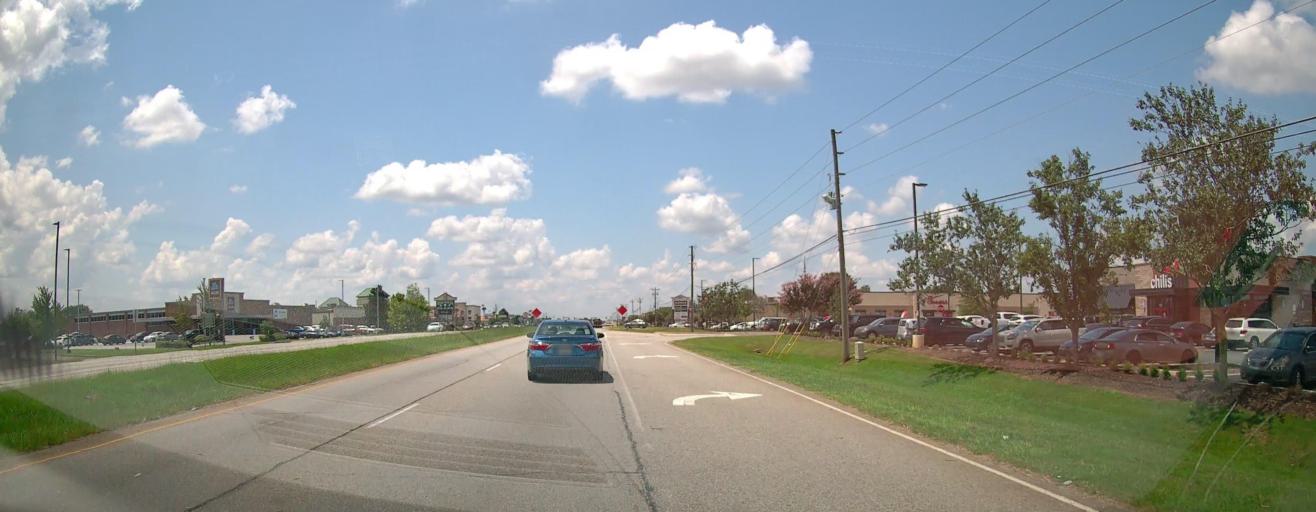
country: US
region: Georgia
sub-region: Houston County
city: Centerville
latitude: 32.6153
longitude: -83.6916
